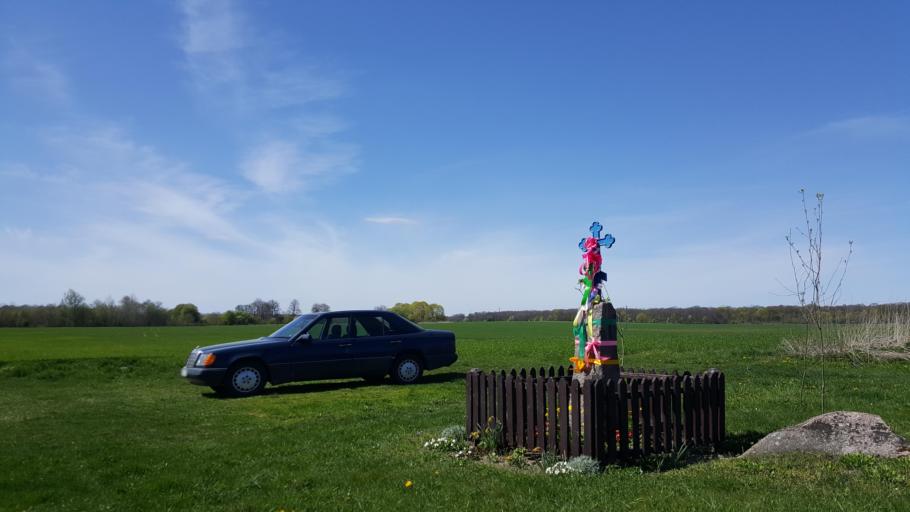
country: BY
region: Brest
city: Vysokaye
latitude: 52.3537
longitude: 23.4378
